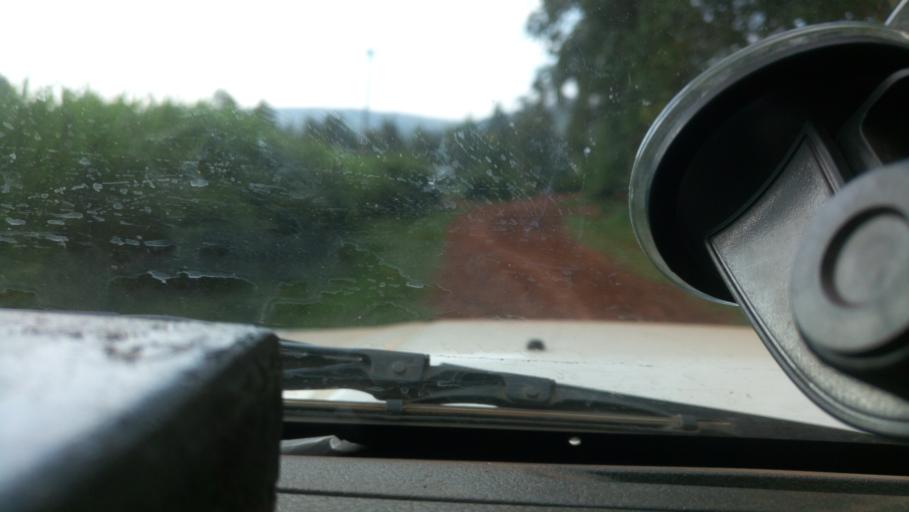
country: KE
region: Kisii
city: Ogembo
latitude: -0.7724
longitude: 34.8168
